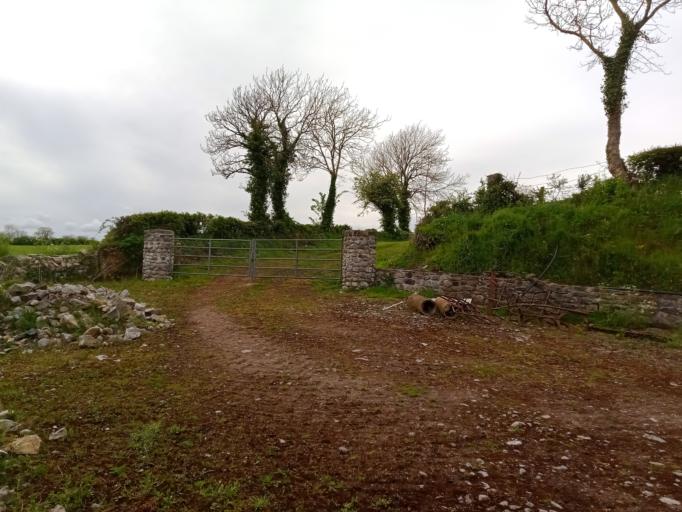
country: IE
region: Leinster
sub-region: Kilkenny
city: Ballyragget
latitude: 52.7226
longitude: -7.4710
